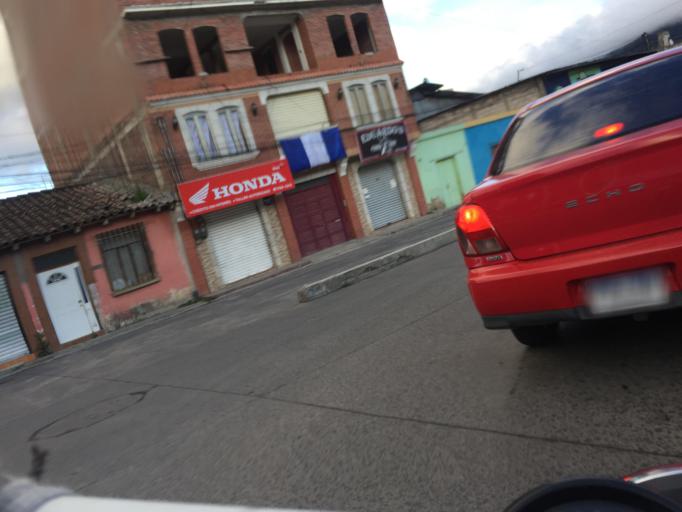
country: GT
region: Totonicapan
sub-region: Municipio de Totonicapan
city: Totonicapan
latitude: 14.9115
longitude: -91.3667
